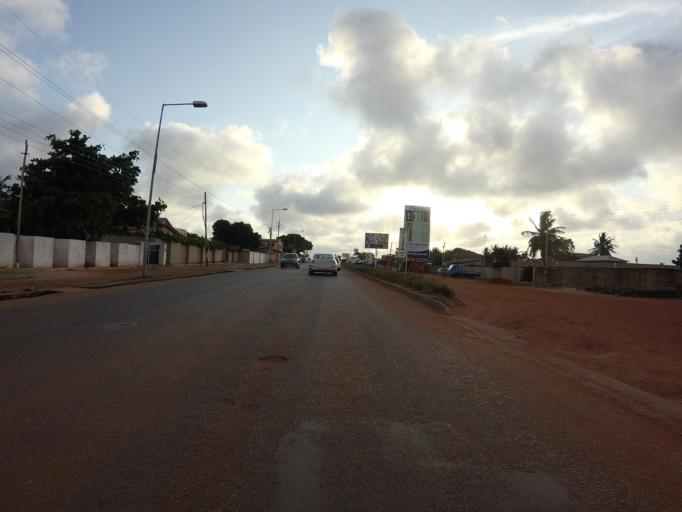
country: GH
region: Greater Accra
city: Teshi Old Town
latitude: 5.6088
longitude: -0.1095
